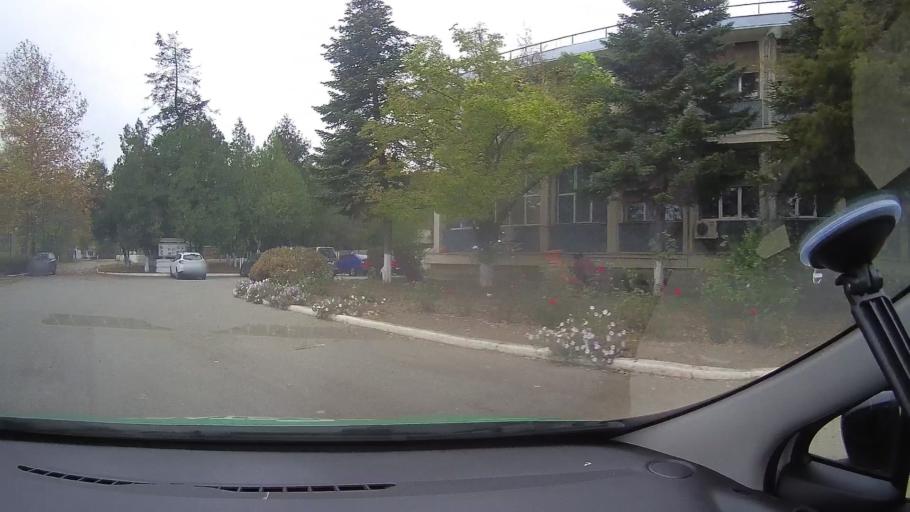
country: RO
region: Constanta
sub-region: Oras Murfatlar
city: Murfatlar
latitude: 44.1770
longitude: 28.4228
